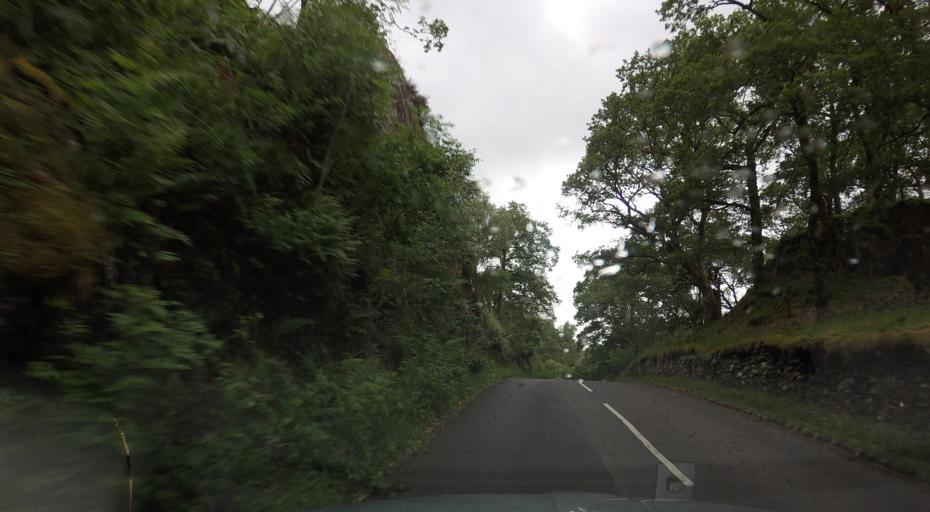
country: GB
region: England
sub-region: Cumbria
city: Keswick
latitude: 54.5442
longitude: -3.1549
